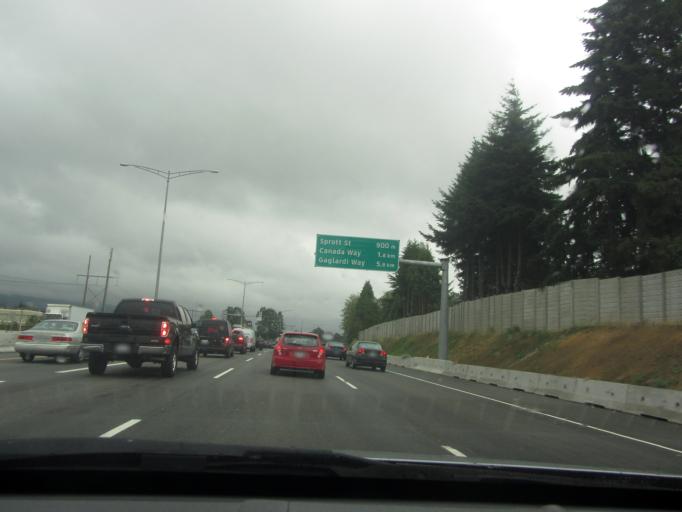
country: CA
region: British Columbia
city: Burnaby
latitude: 49.2577
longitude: -122.9875
